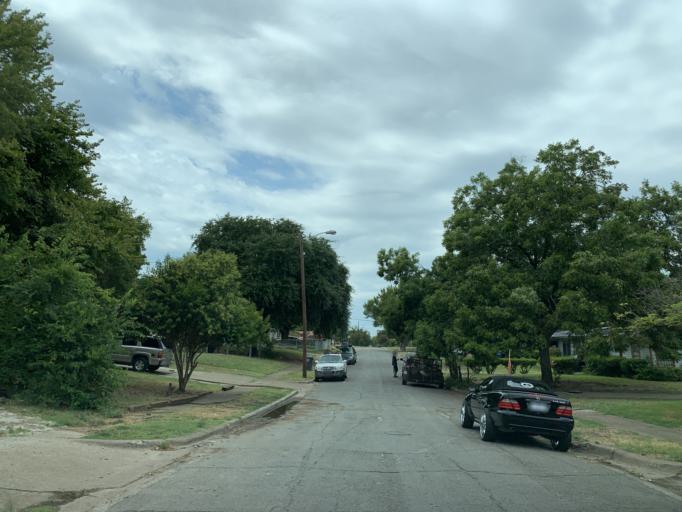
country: US
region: Texas
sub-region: Dallas County
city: DeSoto
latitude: 32.6608
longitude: -96.8334
